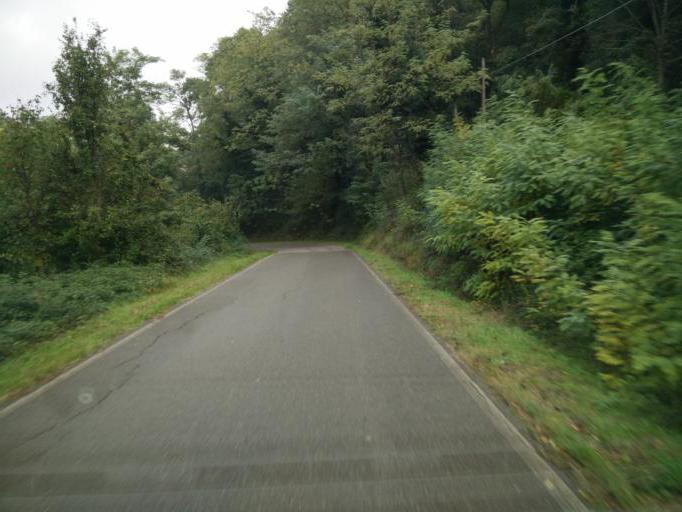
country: IT
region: Emilia-Romagna
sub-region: Provincia di Bologna
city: Marzabotto
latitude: 44.3223
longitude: 11.1868
